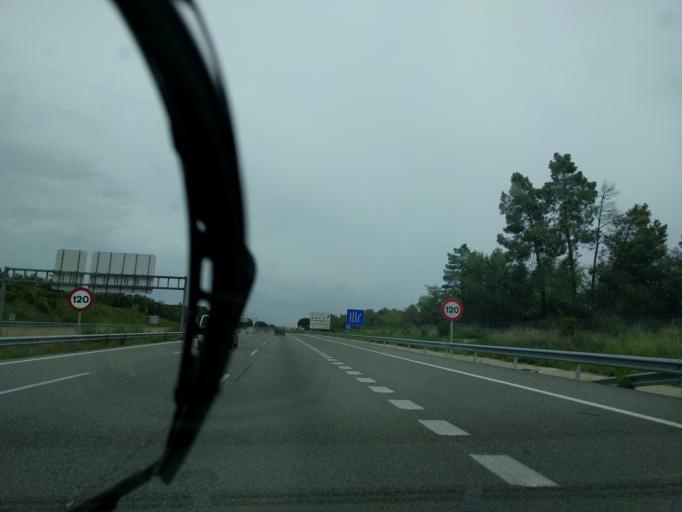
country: ES
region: Catalonia
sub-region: Provincia de Girona
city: Vilobi d'Onyar
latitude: 41.9012
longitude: 2.7743
